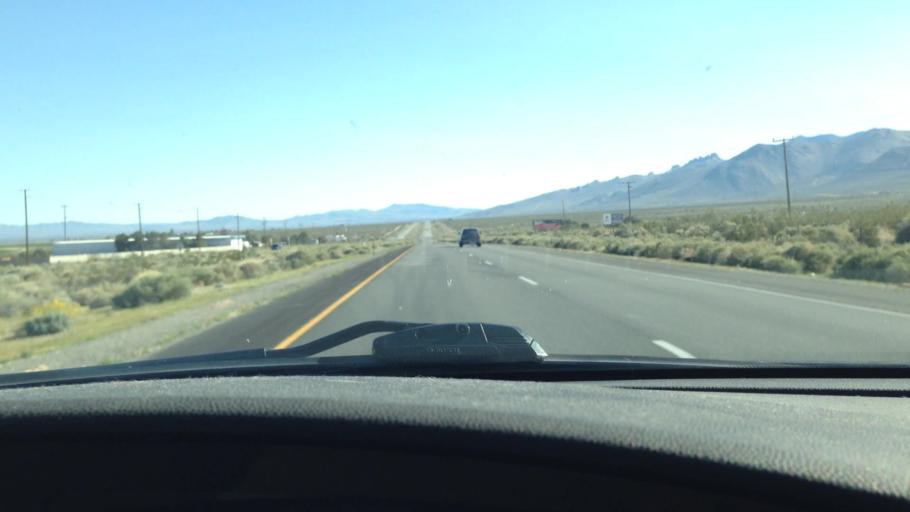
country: US
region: California
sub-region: Kern County
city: Inyokern
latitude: 35.8075
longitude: -117.8734
